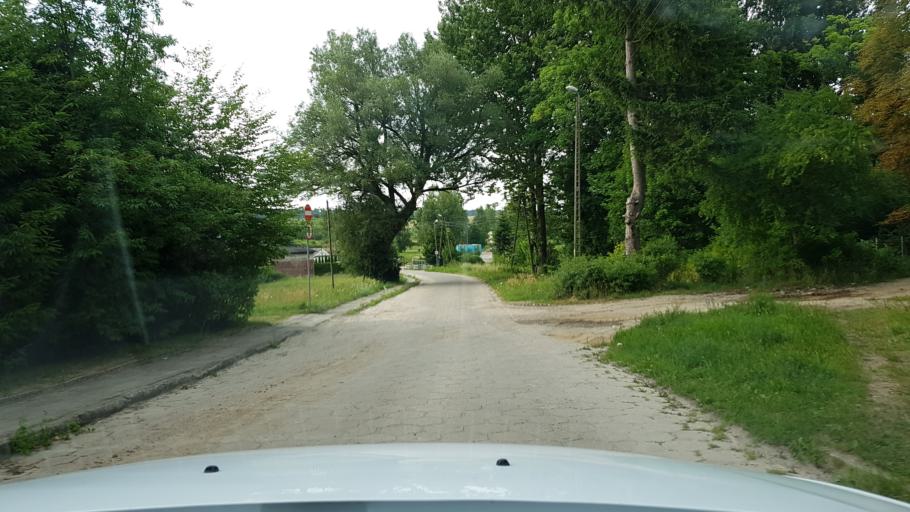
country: PL
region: West Pomeranian Voivodeship
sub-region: Powiat swidwinski
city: Polczyn-Zdroj
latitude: 53.7763
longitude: 16.0942
